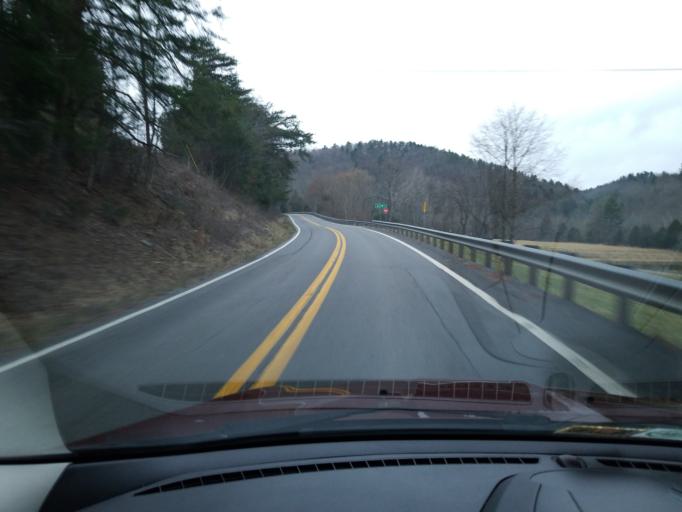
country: US
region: West Virginia
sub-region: Monroe County
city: Union
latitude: 37.5032
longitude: -80.6119
